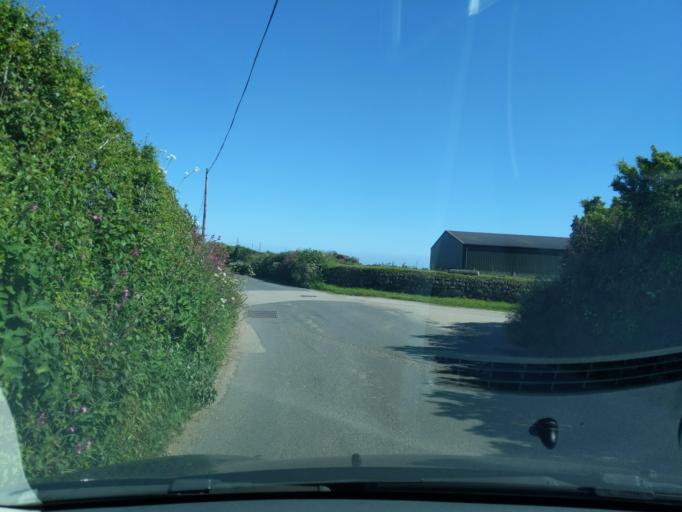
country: GB
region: England
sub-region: Cornwall
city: St. Buryan
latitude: 50.0713
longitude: -5.6128
